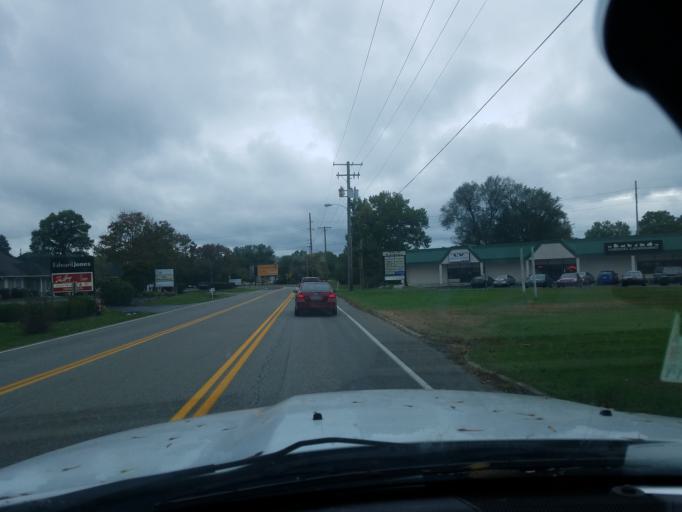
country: US
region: Kentucky
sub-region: Jefferson County
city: Lyndon
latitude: 38.2682
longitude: -85.5799
